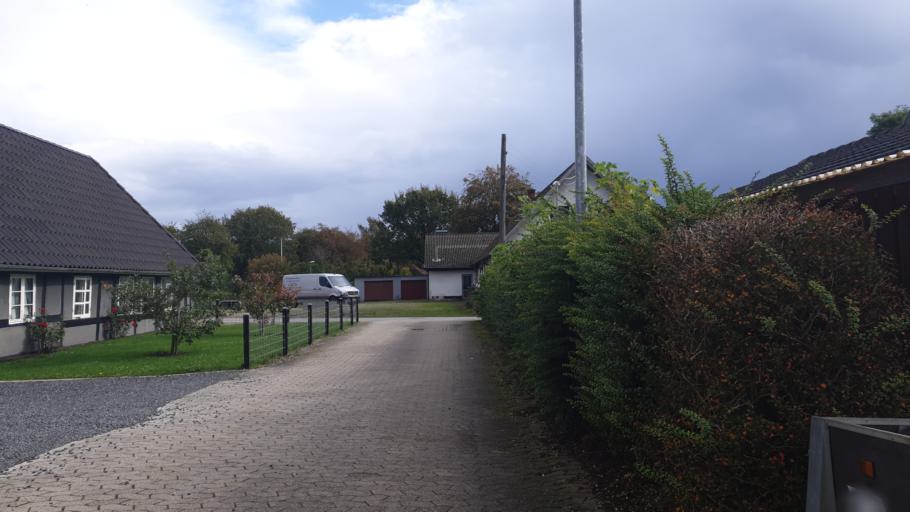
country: DK
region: Central Jutland
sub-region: Hedensted Kommune
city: Hedensted
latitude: 55.8029
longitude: 9.7046
